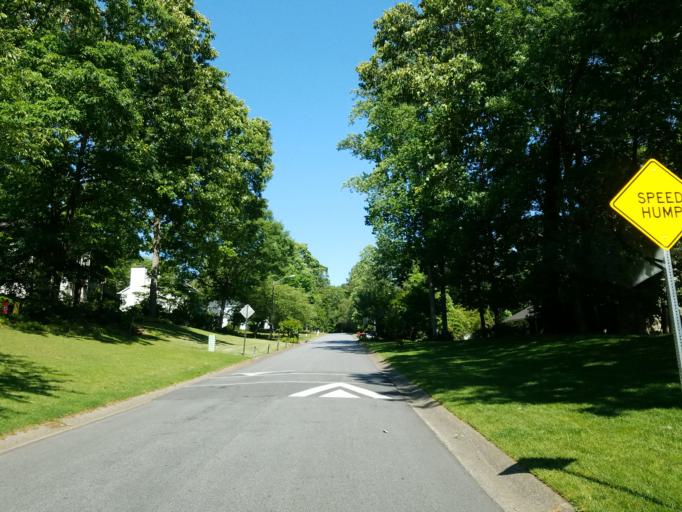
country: US
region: Georgia
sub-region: Cherokee County
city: Woodstock
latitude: 34.0303
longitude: -84.5023
